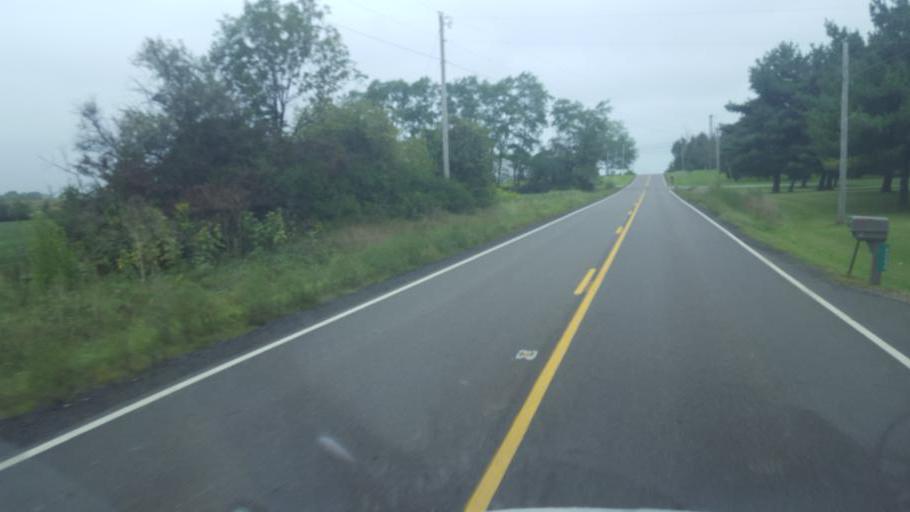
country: US
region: Ohio
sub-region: Knox County
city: Centerburg
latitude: 40.3325
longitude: -82.6910
